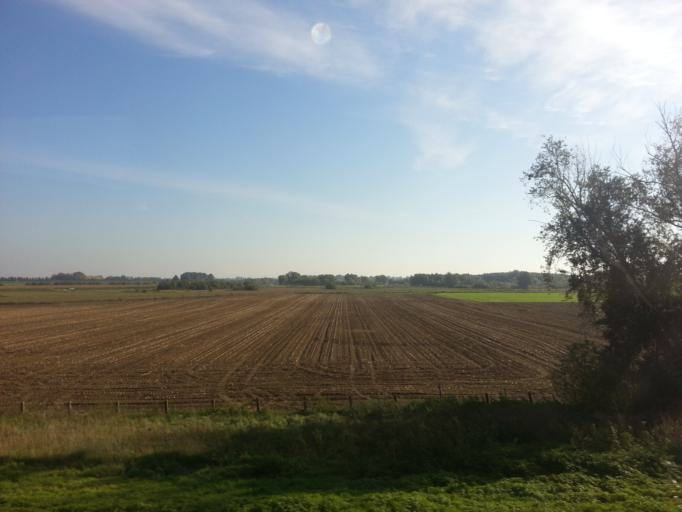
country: NL
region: Gelderland
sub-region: Gemeente Maasdriel
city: Hedel
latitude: 51.7440
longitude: 5.2739
